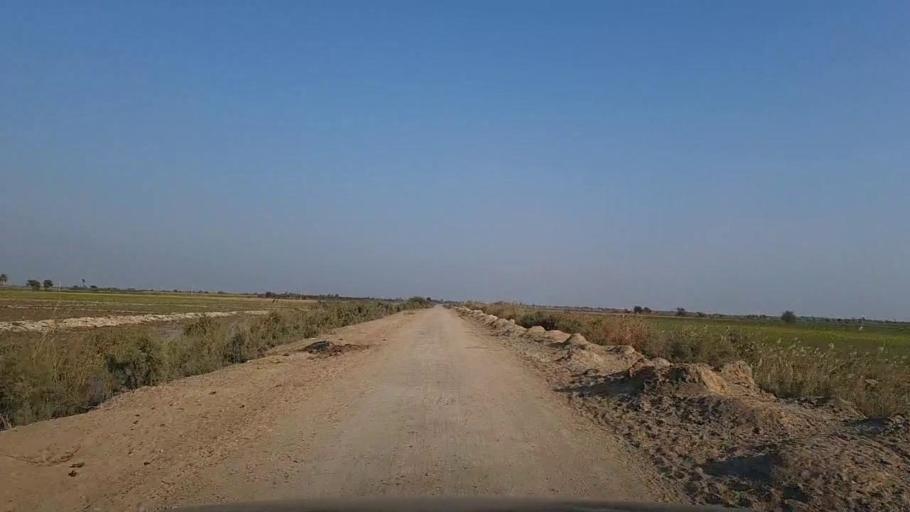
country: PK
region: Sindh
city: Tando Mittha Khan
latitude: 25.9252
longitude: 69.0789
